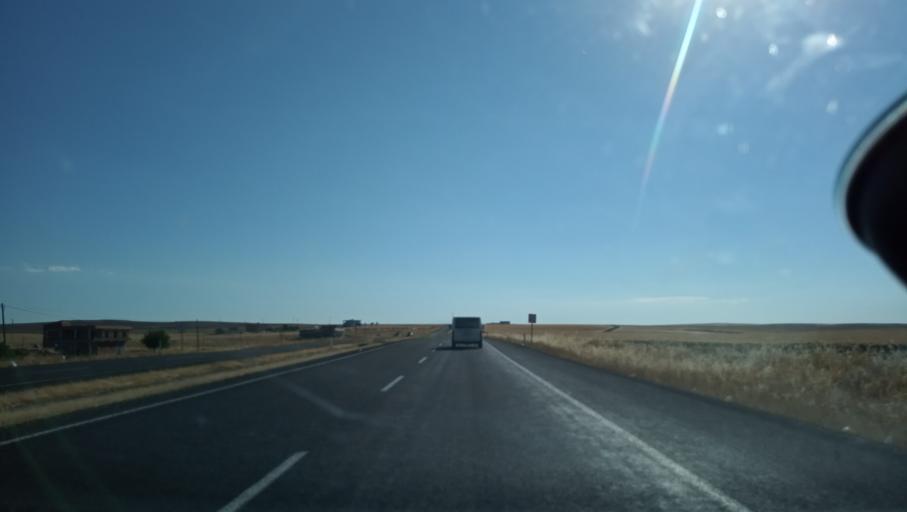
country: TR
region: Diyarbakir
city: Ambar
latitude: 37.9993
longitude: 40.4147
